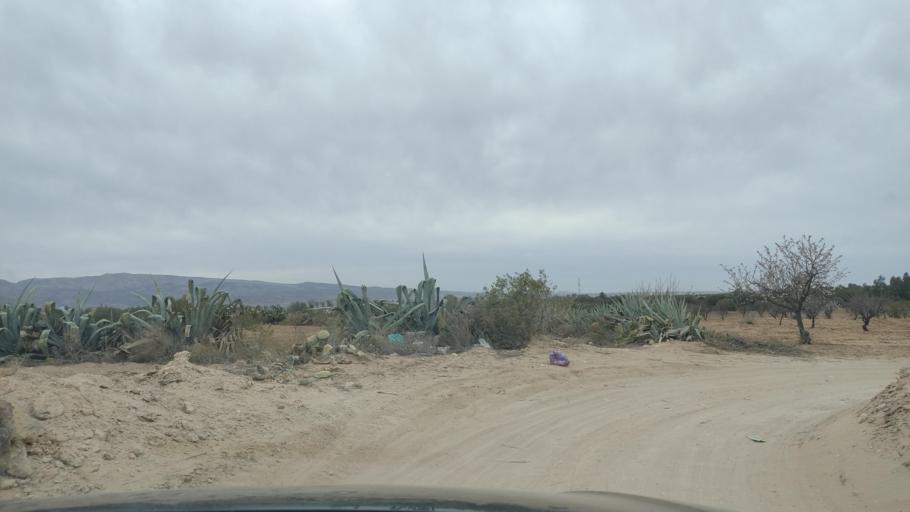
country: TN
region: Al Qasrayn
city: Kasserine
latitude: 35.2256
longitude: 8.9209
